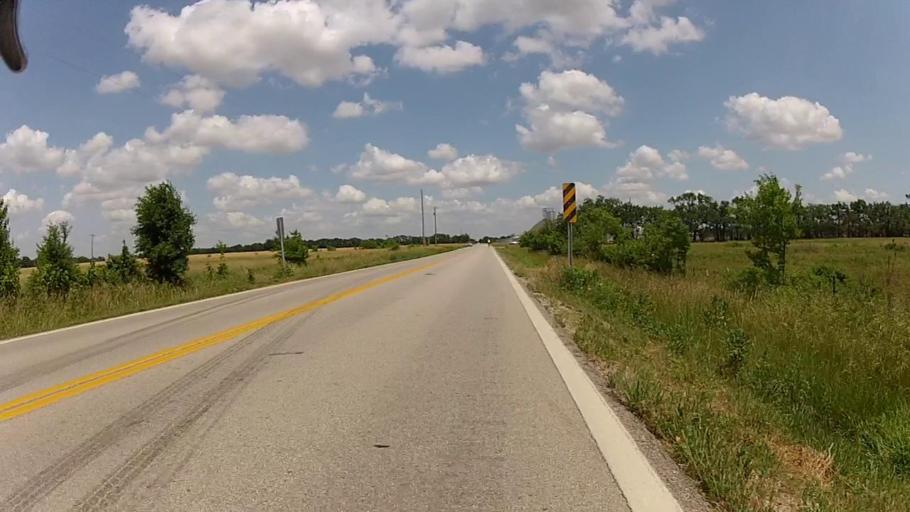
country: US
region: Kansas
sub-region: Labette County
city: Altamont
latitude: 37.1926
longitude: -95.3414
